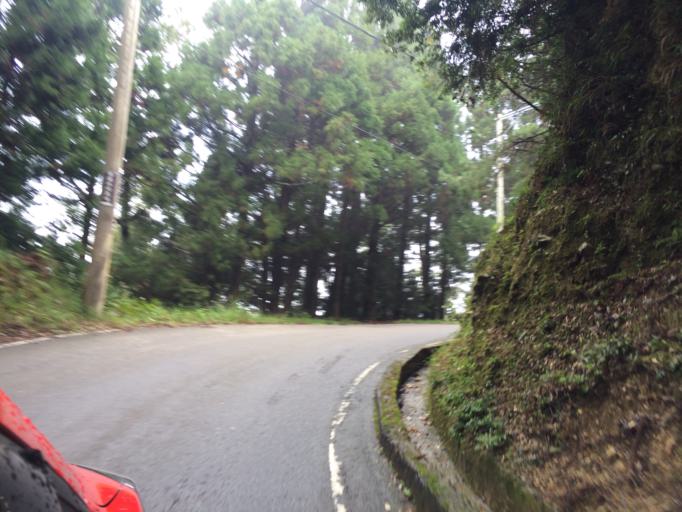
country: TW
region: Taiwan
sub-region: Miaoli
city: Miaoli
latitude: 24.5264
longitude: 121.1134
